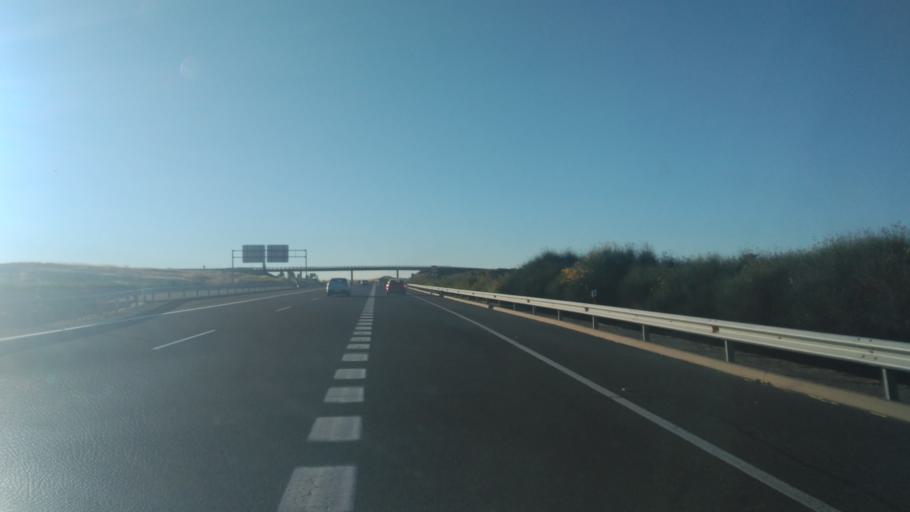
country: ES
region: Castille and Leon
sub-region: Provincia de Salamanca
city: Carbajosa de la Sagrada
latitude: 40.9195
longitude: -5.6649
